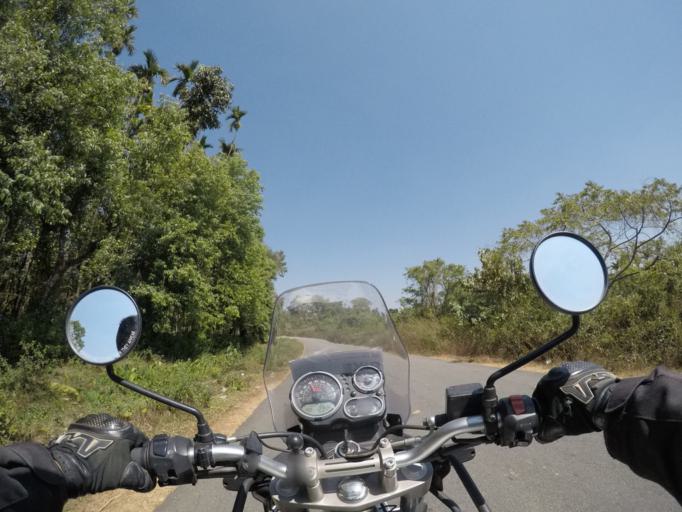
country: IN
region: Karnataka
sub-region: Chikmagalur
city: Mudigere
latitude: 13.0440
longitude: 75.6876
